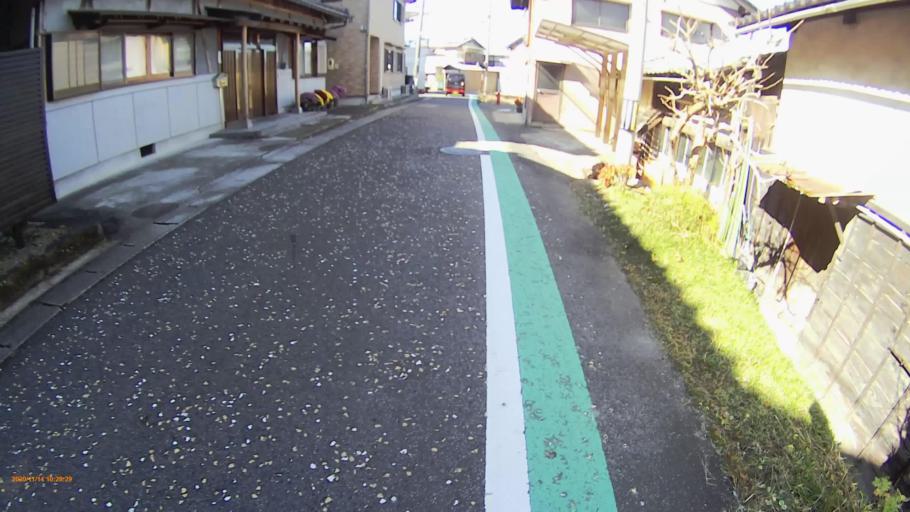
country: JP
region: Gifu
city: Nakatsugawa
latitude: 35.5104
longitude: 137.5333
